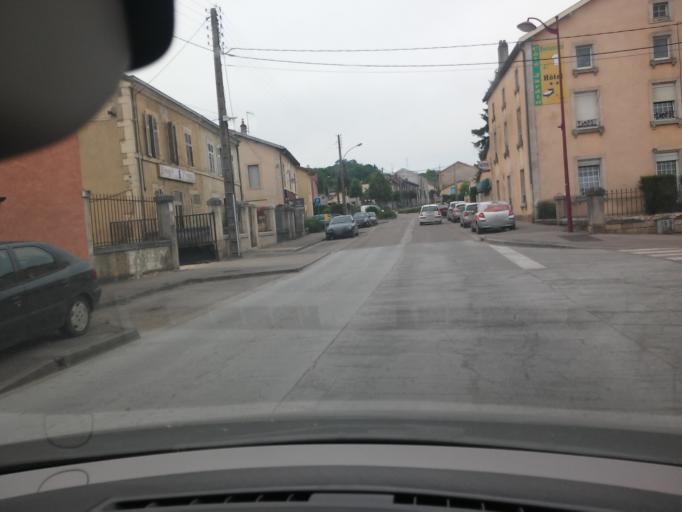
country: FR
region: Lorraine
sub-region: Departement de la Meuse
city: Commercy
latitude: 48.7654
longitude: 5.5831
